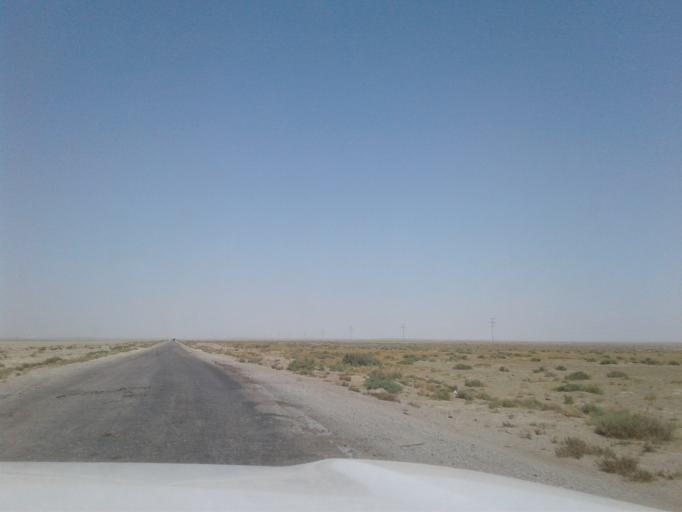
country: TM
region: Balkan
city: Gumdag
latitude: 38.3316
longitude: 54.3543
